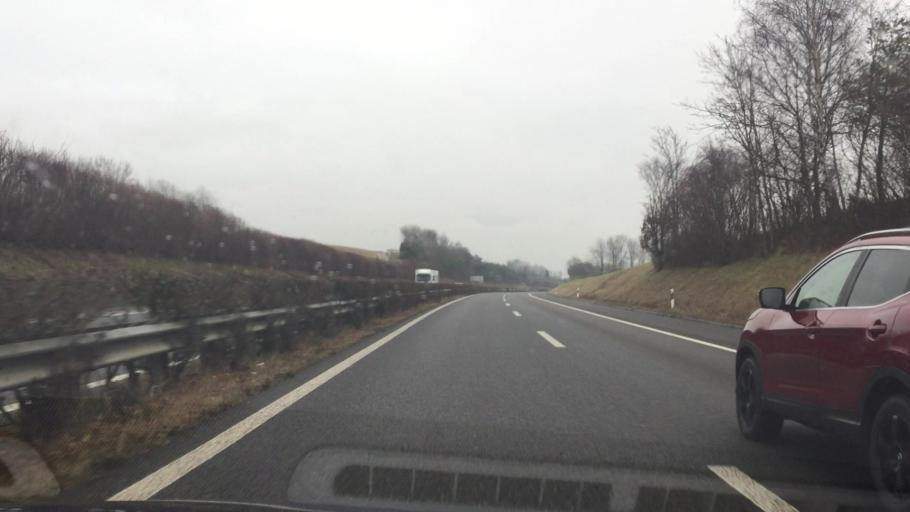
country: CH
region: Vaud
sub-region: Jura-Nord vaudois District
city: Montagny
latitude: 46.8012
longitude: 6.6230
